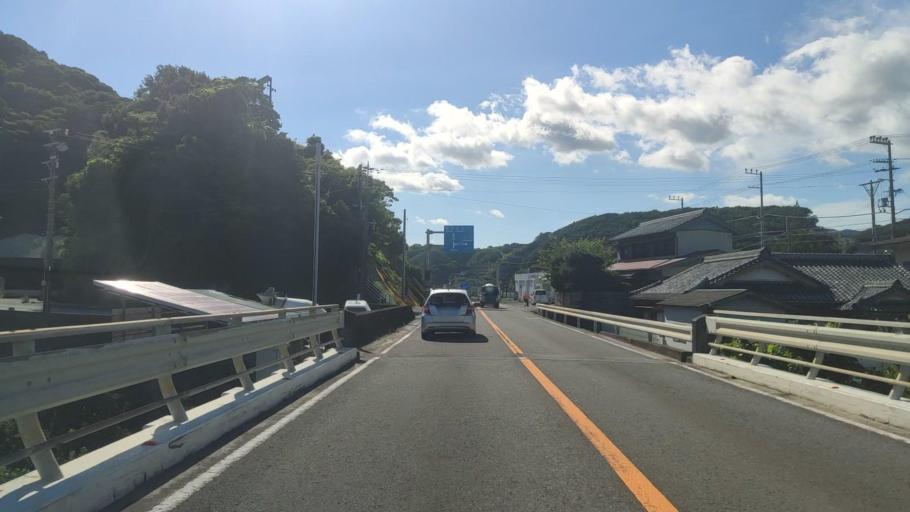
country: JP
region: Wakayama
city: Shingu
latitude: 33.4827
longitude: 135.7649
